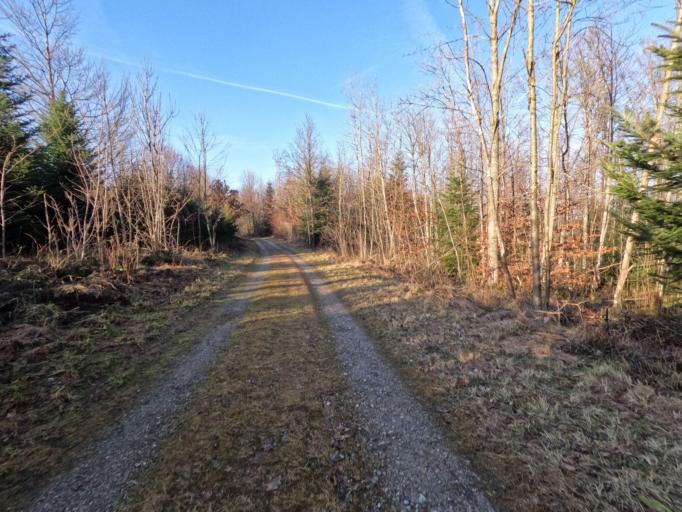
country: DE
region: Bavaria
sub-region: Upper Bavaria
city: Traunstein
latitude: 47.8945
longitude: 12.6287
